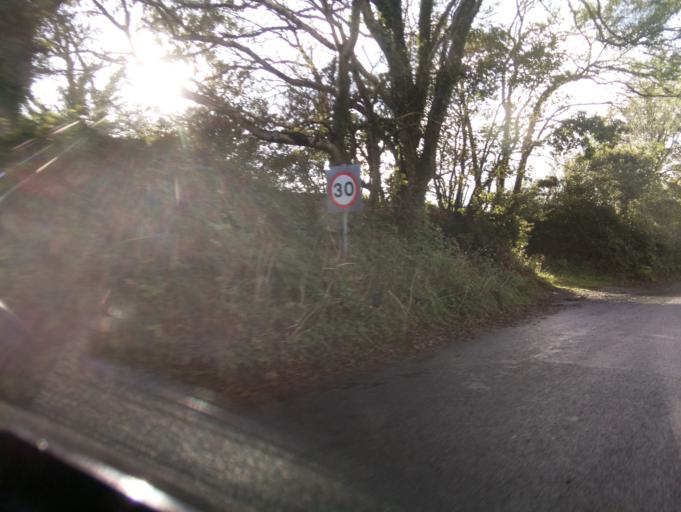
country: GB
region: England
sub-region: Devon
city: Totnes
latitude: 50.3595
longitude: -3.7318
